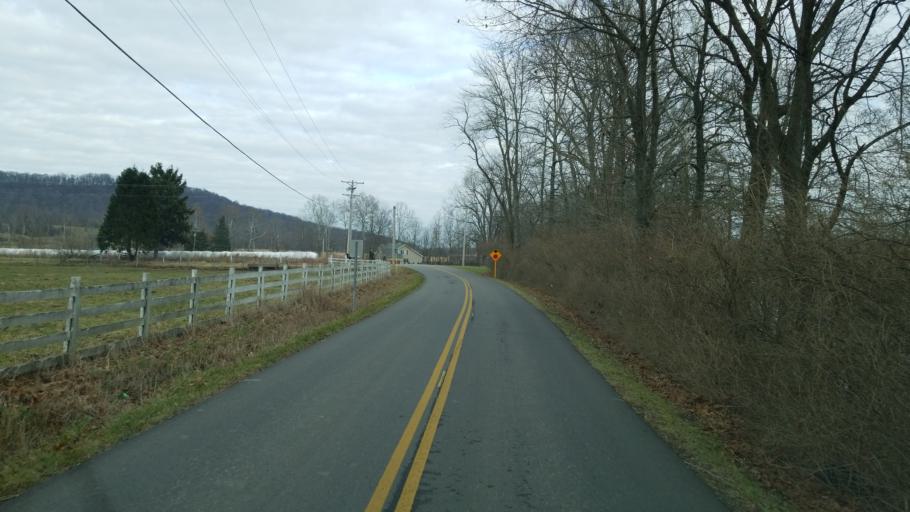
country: US
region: Ohio
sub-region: Highland County
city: Greenfield
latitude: 39.2363
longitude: -83.2808
